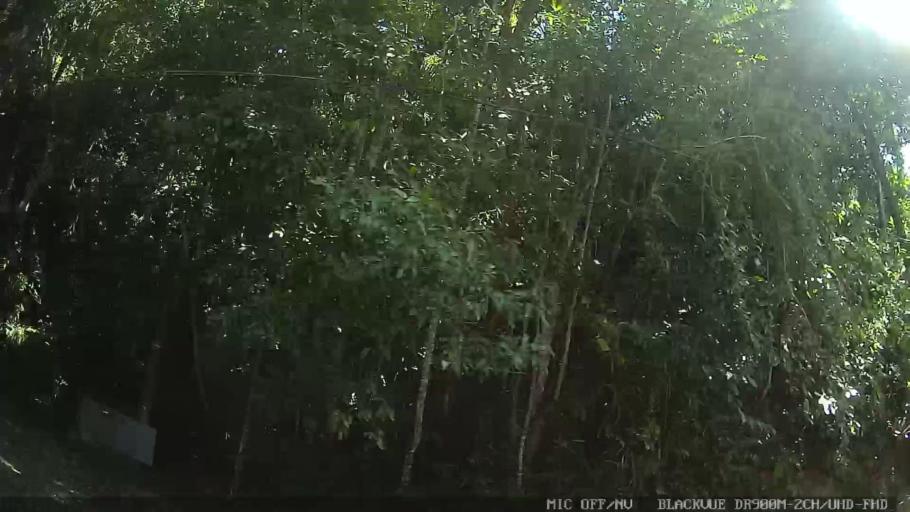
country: BR
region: Sao Paulo
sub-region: Guaruja
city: Guaruja
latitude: -23.9851
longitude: -46.1886
